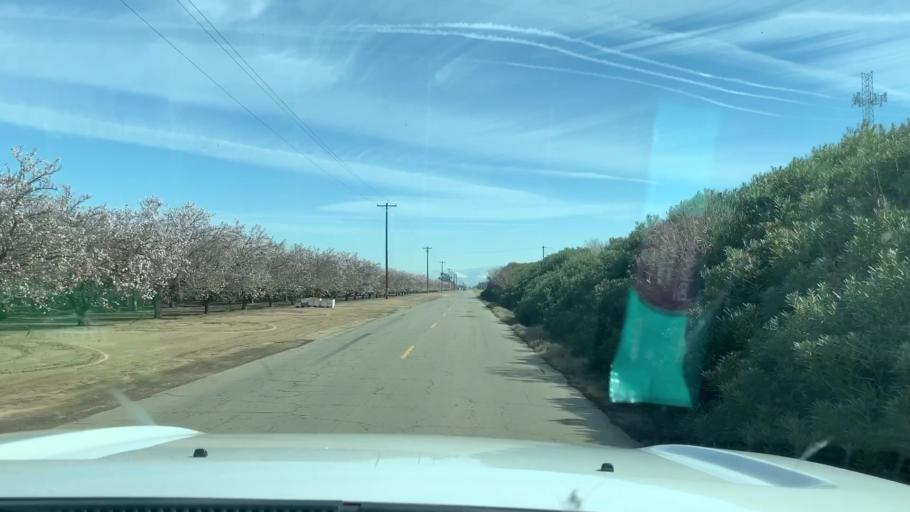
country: US
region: California
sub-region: Kern County
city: Shafter
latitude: 35.4853
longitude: -119.2673
